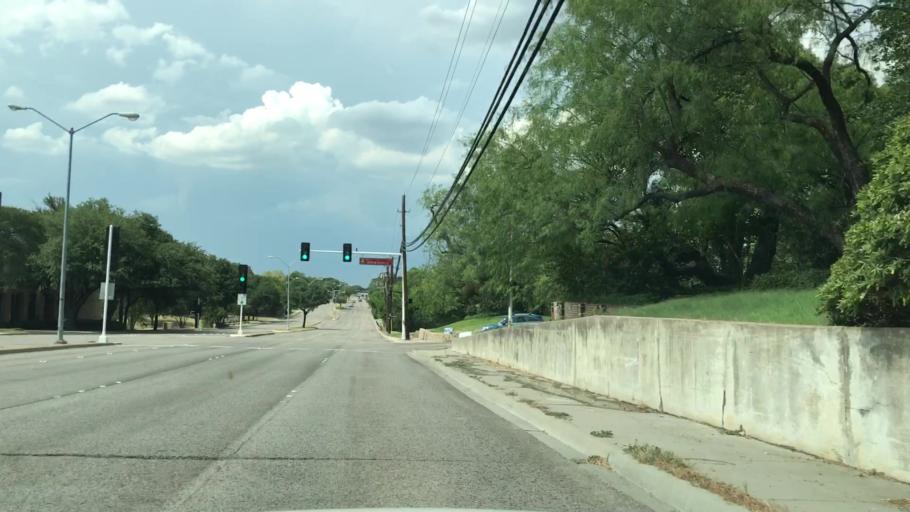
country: US
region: Texas
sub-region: Dallas County
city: Farmers Branch
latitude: 32.9326
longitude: -96.8730
